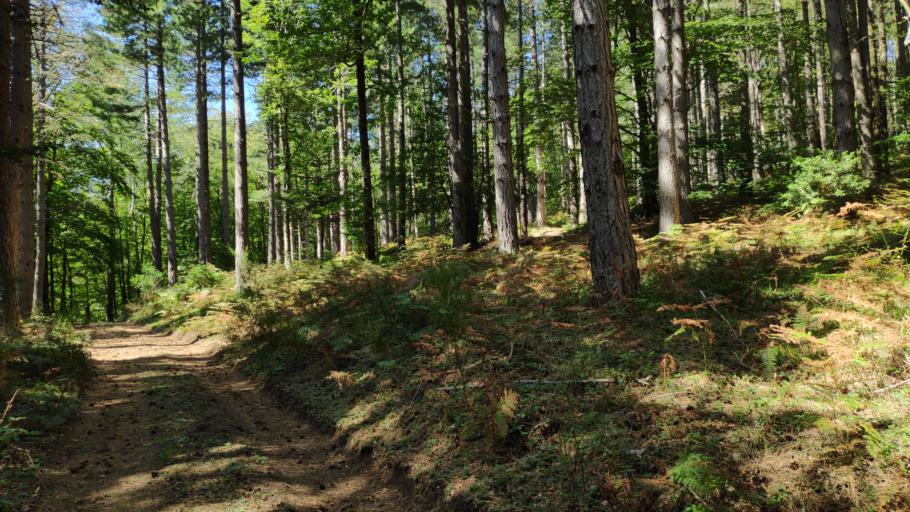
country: IT
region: Calabria
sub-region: Provincia di Vibo-Valentia
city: Nardodipace
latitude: 38.5251
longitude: 16.3843
